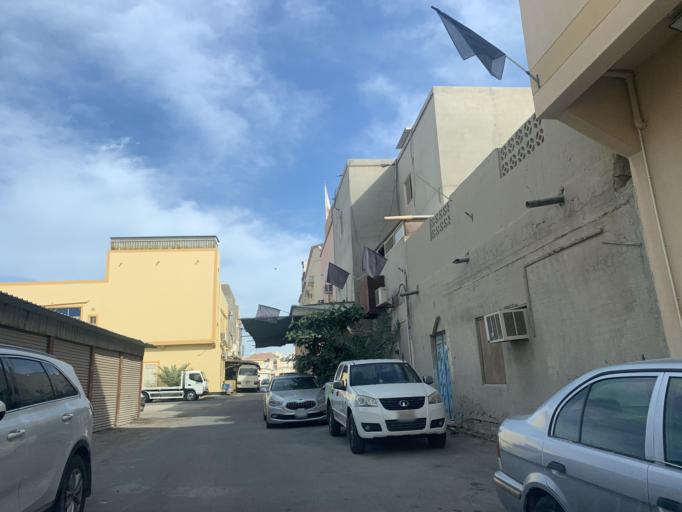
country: BH
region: Central Governorate
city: Madinat Hamad
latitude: 26.1233
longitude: 50.4765
